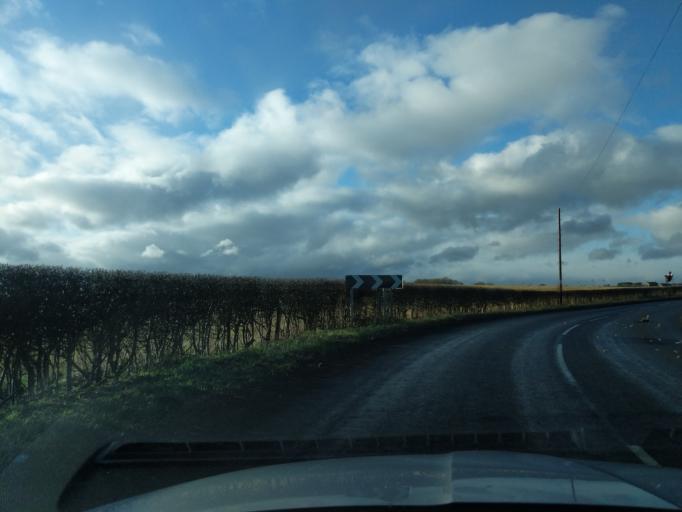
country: GB
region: England
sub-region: North Yorkshire
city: Catterick
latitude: 54.3125
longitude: -1.6722
